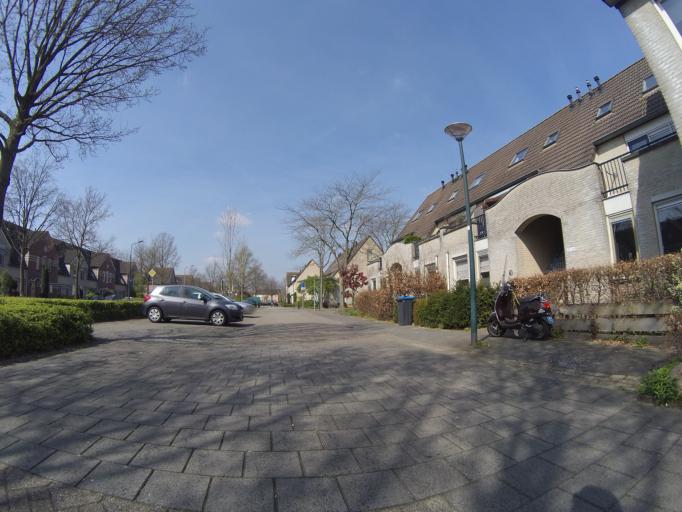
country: NL
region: North Holland
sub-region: Gemeente Blaricum
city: Blaricum
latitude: 52.2488
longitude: 5.2605
